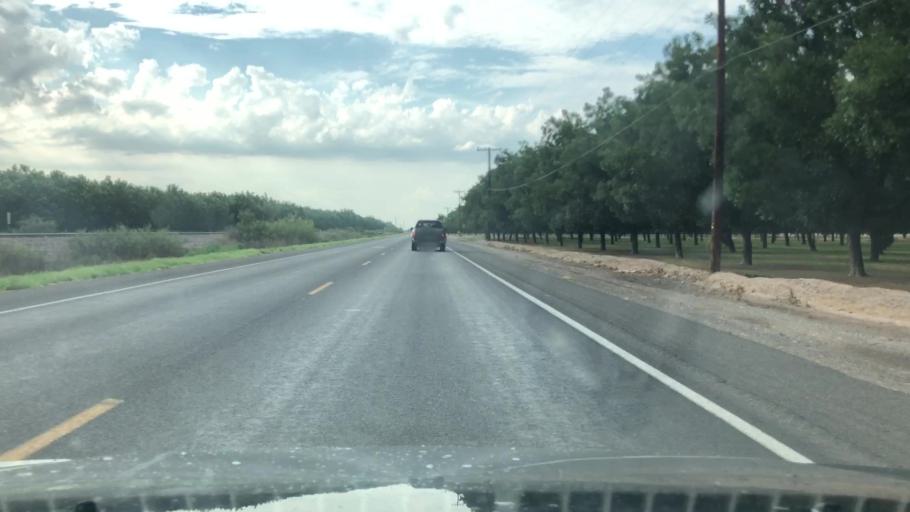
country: US
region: New Mexico
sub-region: Dona Ana County
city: Mesquite
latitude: 32.2126
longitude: -106.7269
